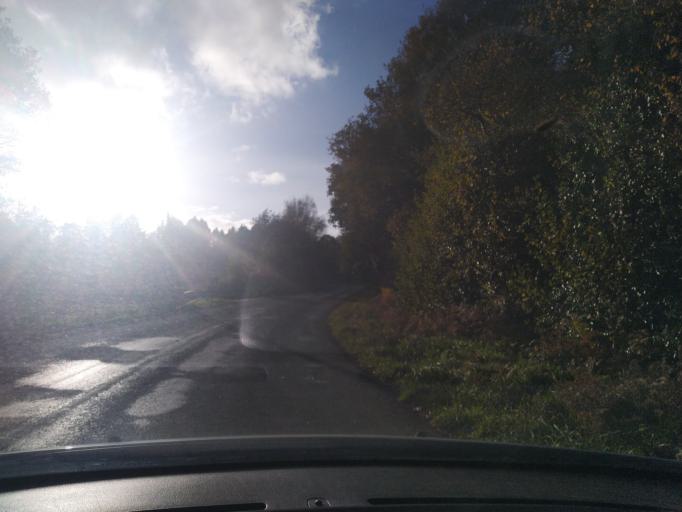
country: FR
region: Brittany
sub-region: Departement du Finistere
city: Plouigneau
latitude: 48.5724
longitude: -3.6597
